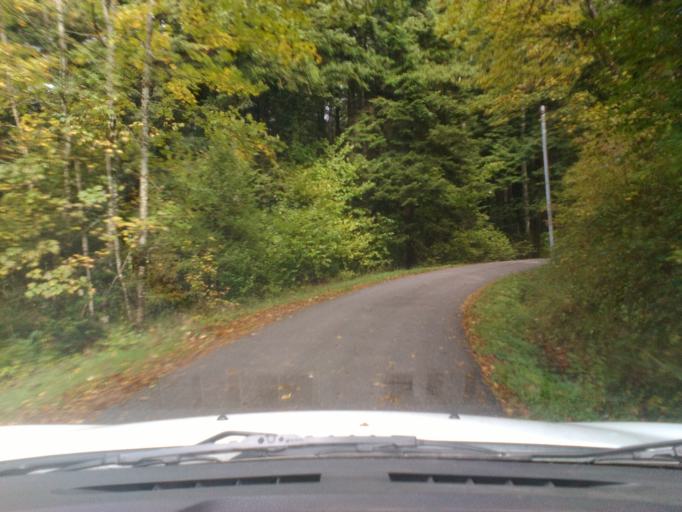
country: FR
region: Lorraine
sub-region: Departement des Vosges
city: Saint-Die-des-Vosges
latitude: 48.3099
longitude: 6.9753
